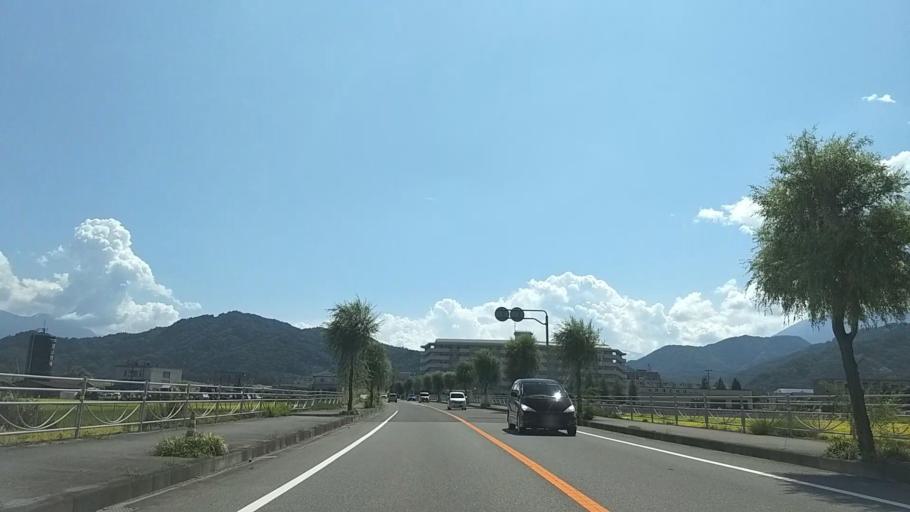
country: JP
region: Yamanashi
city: Ryuo
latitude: 35.5535
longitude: 138.4682
